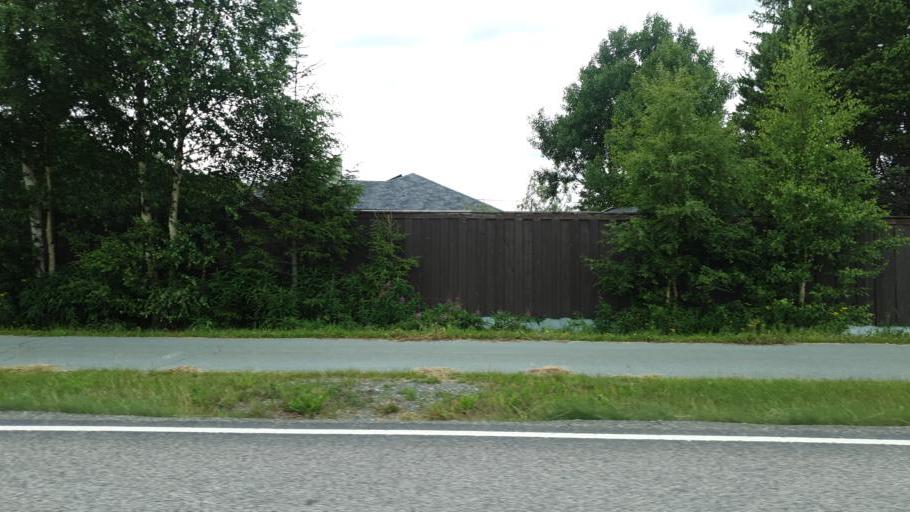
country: NO
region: Sor-Trondelag
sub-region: Oppdal
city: Oppdal
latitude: 62.5769
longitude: 9.6545
